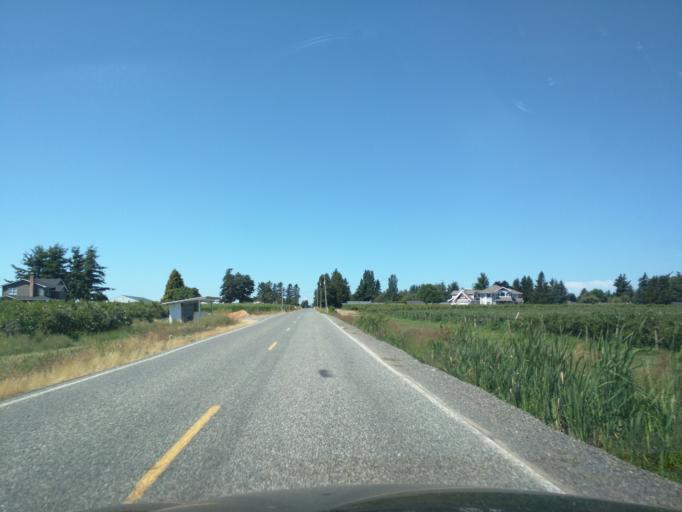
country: US
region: Washington
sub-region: Whatcom County
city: Lynden
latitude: 48.8845
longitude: -122.4458
